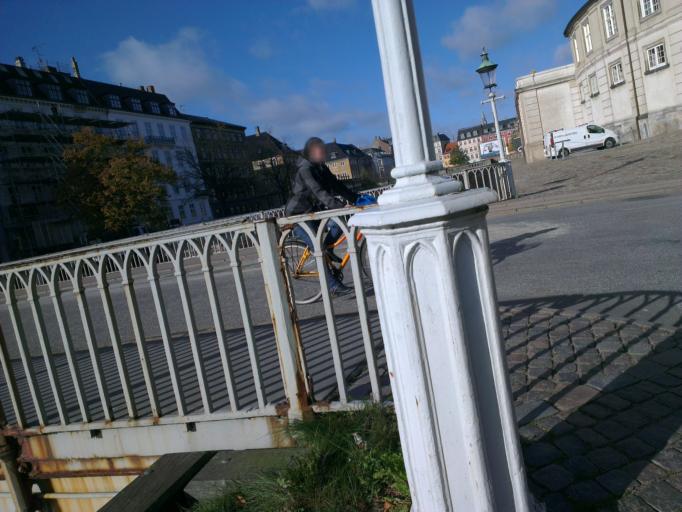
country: DK
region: Capital Region
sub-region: Kobenhavn
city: Copenhagen
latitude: 55.6742
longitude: 12.5778
